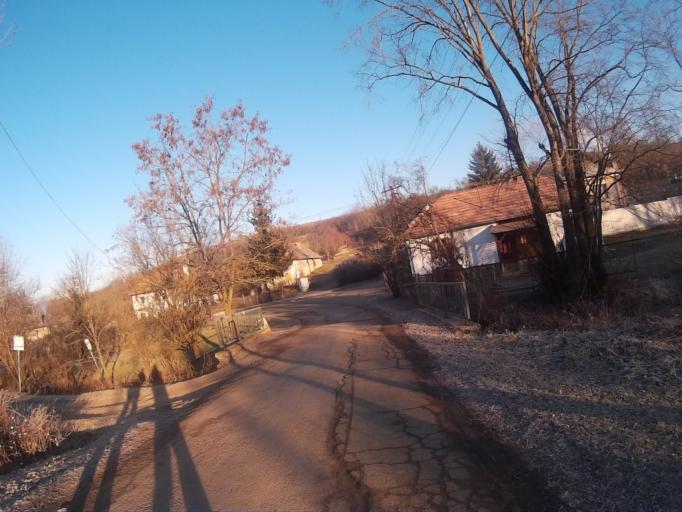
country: HU
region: Borsod-Abauj-Zemplen
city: Putnok
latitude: 48.3557
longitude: 20.4392
